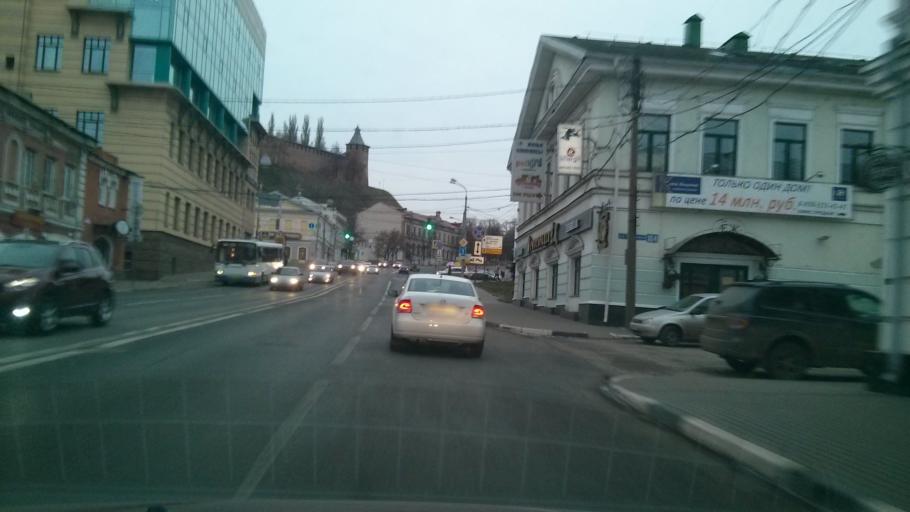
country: RU
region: Nizjnij Novgorod
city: Nizhniy Novgorod
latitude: 56.3307
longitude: 43.9956
